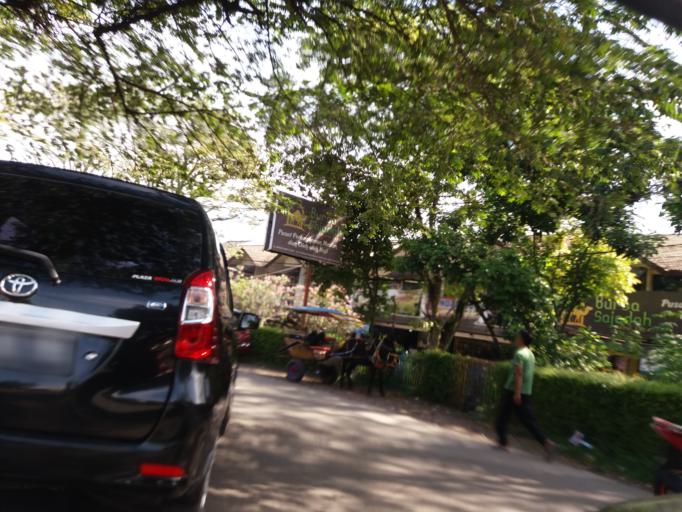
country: ID
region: West Java
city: Bandung
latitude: -6.9410
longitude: 107.6034
